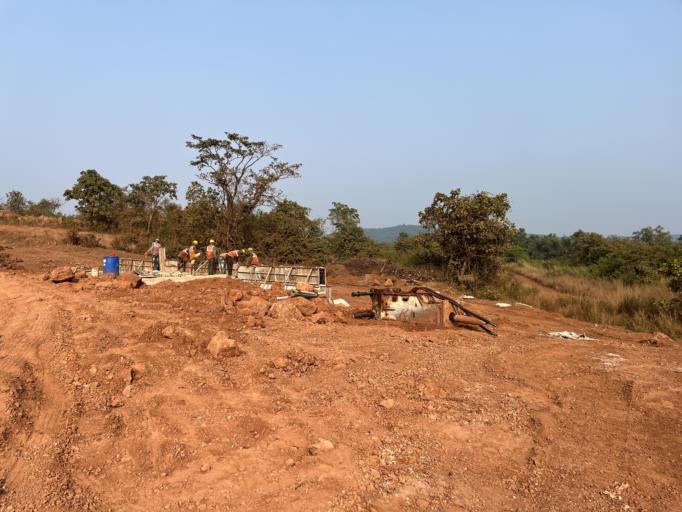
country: IN
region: Goa
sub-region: North Goa
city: Pernem
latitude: 15.6926
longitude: 73.8385
